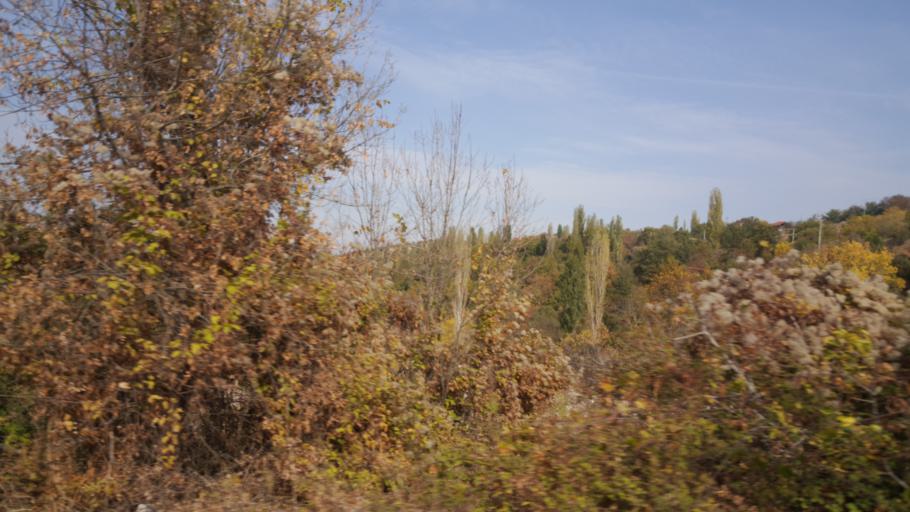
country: TR
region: Eskisehir
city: Mihaliccik
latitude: 39.9760
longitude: 31.3690
